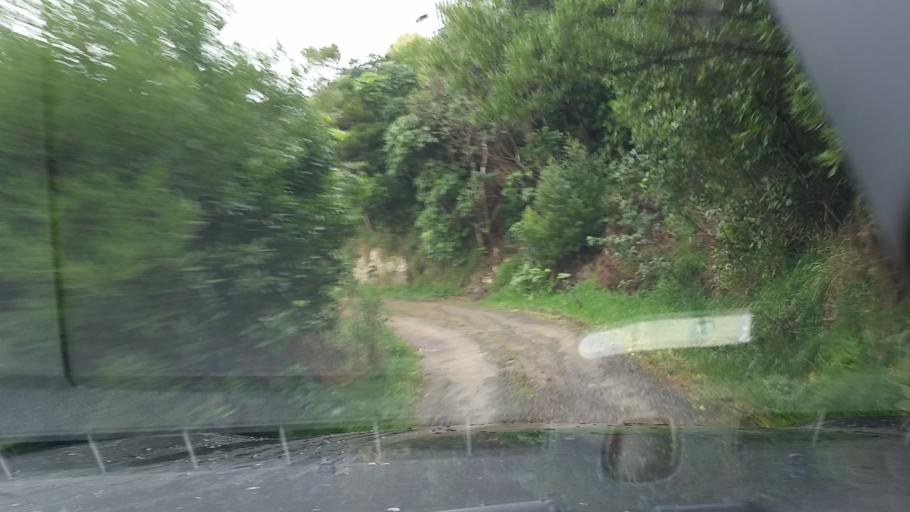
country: NZ
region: Marlborough
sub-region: Marlborough District
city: Picton
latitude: -41.2647
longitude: 174.0372
